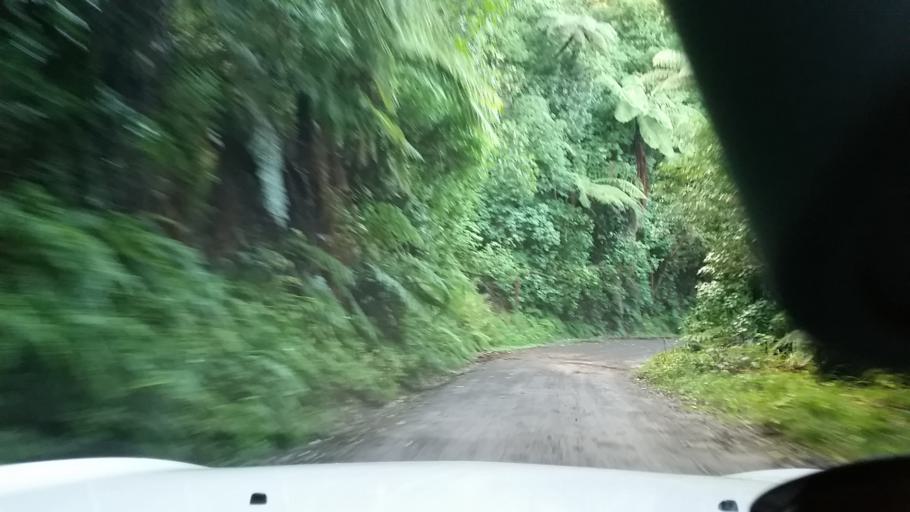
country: NZ
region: Bay of Plenty
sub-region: Kawerau District
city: Kawerau
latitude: -38.0174
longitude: 176.5912
